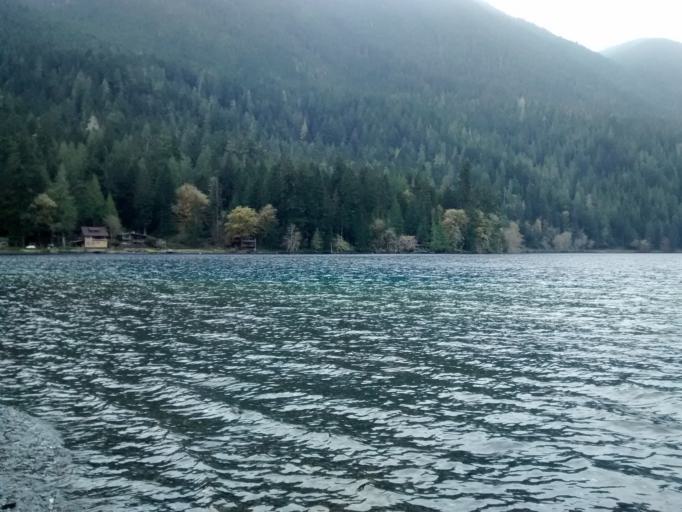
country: CA
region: British Columbia
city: Sooke
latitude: 48.0544
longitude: -123.7999
